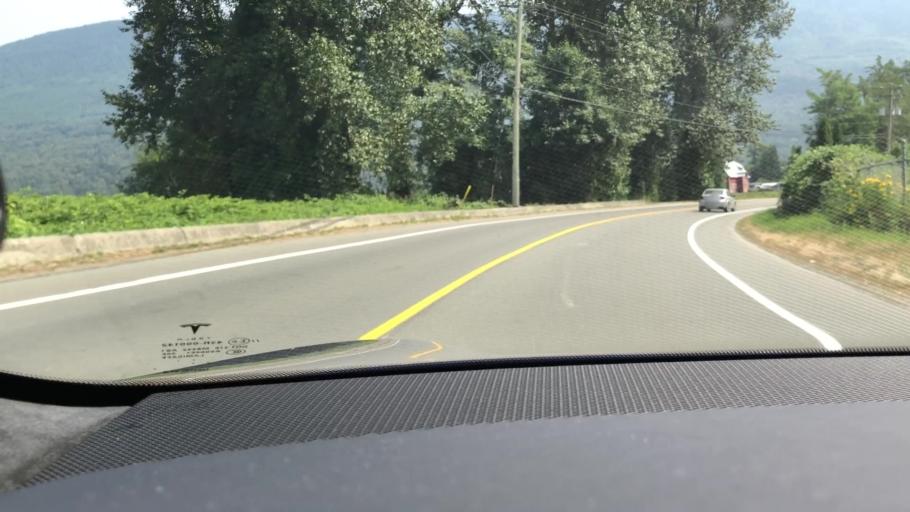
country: CA
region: British Columbia
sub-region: Fraser Valley Regional District
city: Chilliwack
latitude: 49.0886
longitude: -122.0651
